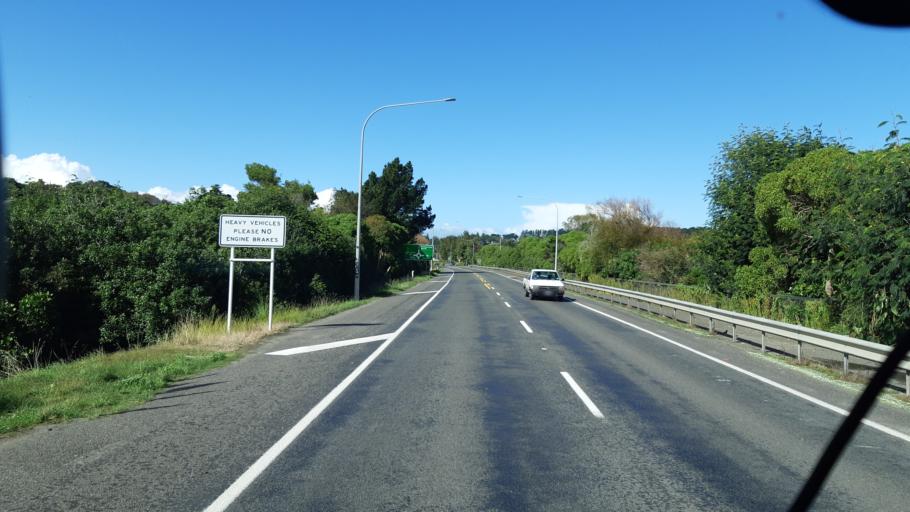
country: NZ
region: Manawatu-Wanganui
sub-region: Wanganui District
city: Wanganui
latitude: -39.9463
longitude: 175.0477
